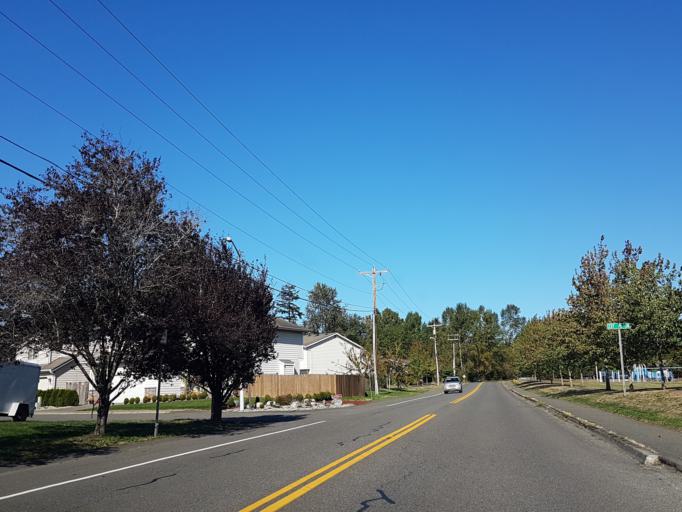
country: US
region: Washington
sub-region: Snohomish County
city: Brier
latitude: 47.7825
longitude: -122.2510
